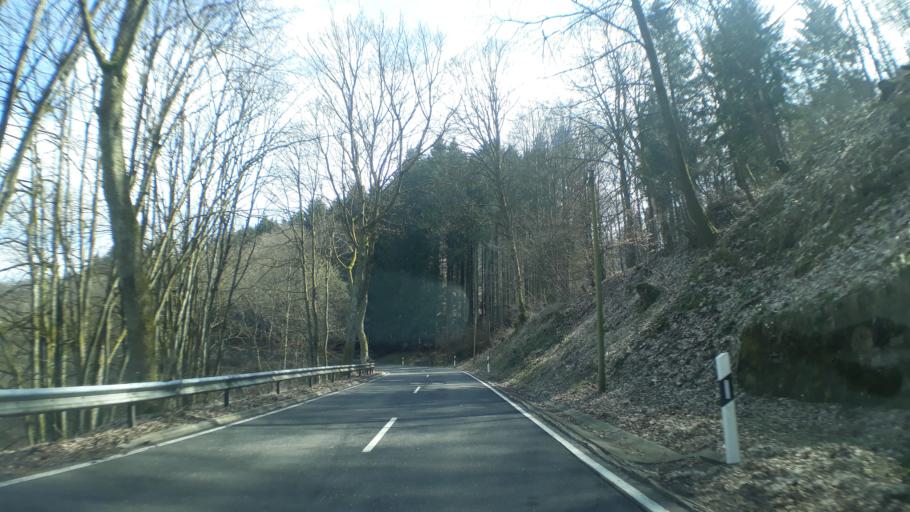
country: DE
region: North Rhine-Westphalia
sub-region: Regierungsbezirk Koln
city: Monschau
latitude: 50.5509
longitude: 6.2541
